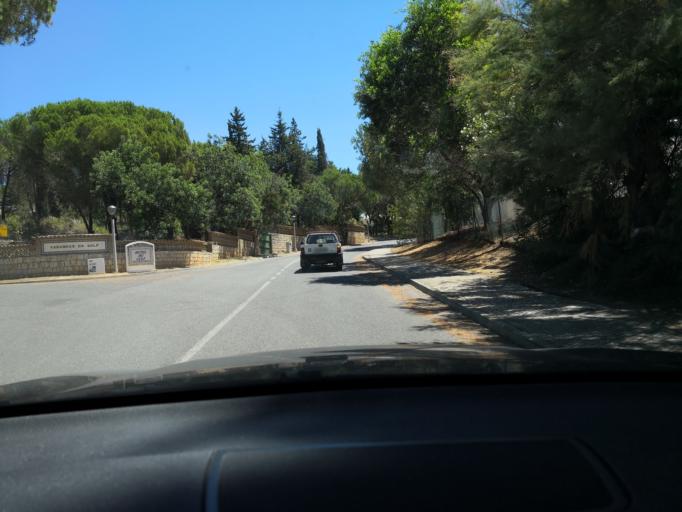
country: PT
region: Faro
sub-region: Loule
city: Vilamoura
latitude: 37.1034
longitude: -8.1178
